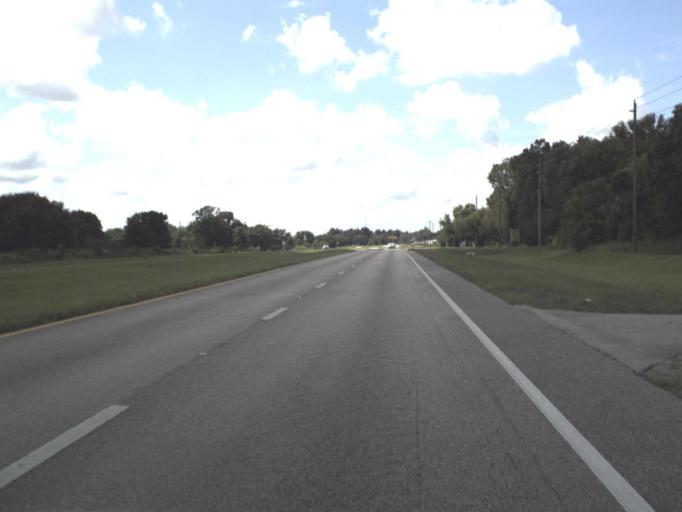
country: US
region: Florida
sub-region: DeSoto County
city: Arcadia
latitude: 27.2525
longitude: -81.8443
